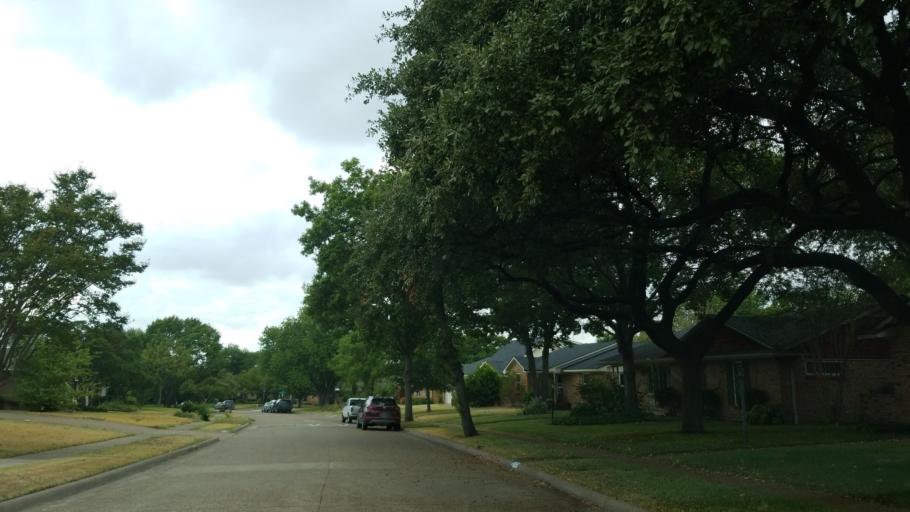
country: US
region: Texas
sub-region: Dallas County
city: Richardson
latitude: 32.9346
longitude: -96.7706
